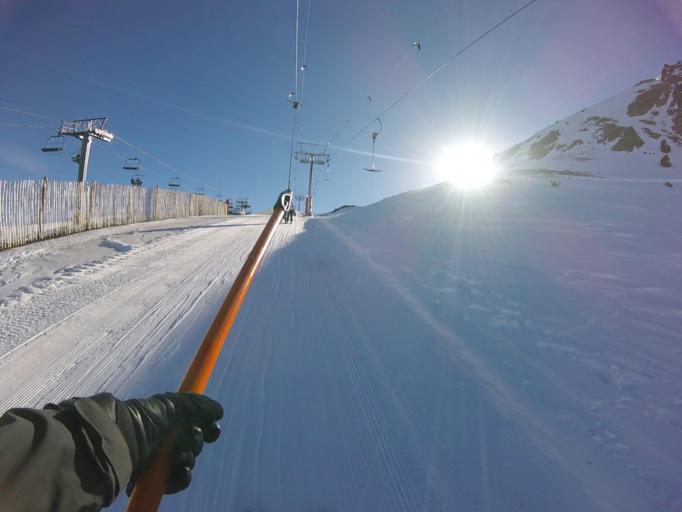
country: AD
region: Canillo
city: El Tarter
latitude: 42.5349
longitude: 1.6809
